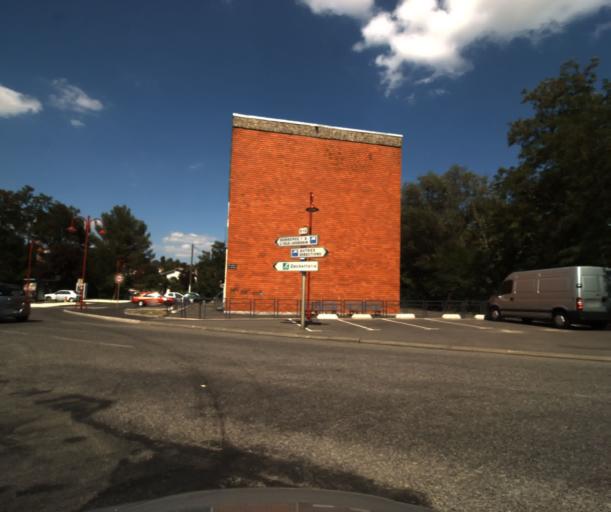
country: FR
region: Midi-Pyrenees
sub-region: Departement de la Haute-Garonne
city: Saint-Lys
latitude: 43.5154
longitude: 1.1751
